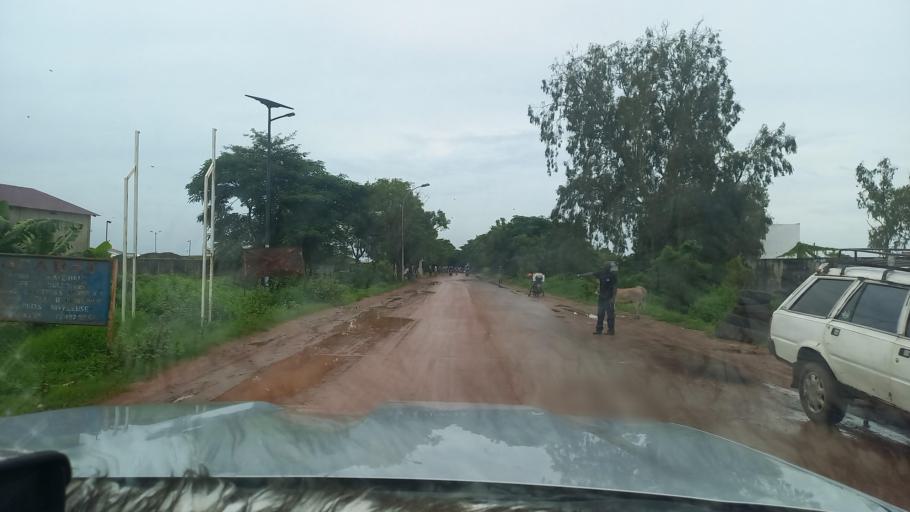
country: SN
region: Ziguinchor
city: Ziguinchor
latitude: 12.5832
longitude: -16.2636
